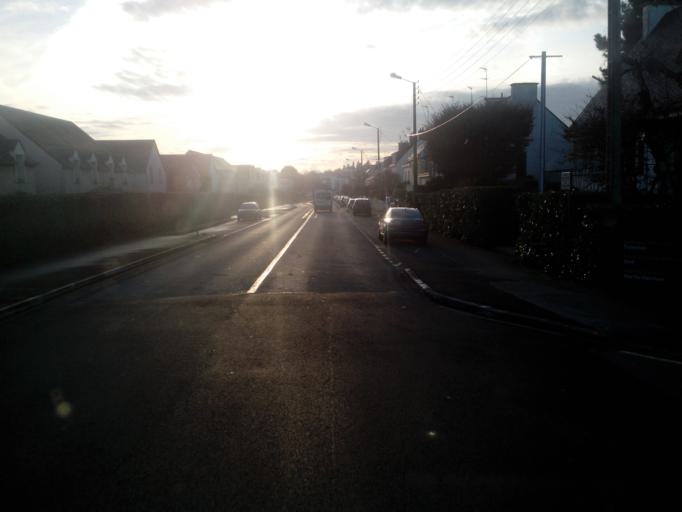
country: FR
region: Brittany
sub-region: Departement du Morbihan
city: Hennebont
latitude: 47.8059
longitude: -3.2600
